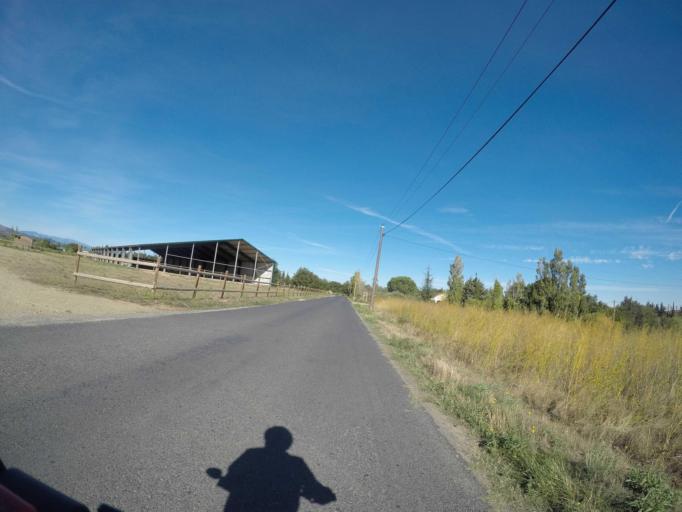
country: FR
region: Languedoc-Roussillon
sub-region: Departement des Pyrenees-Orientales
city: Ponteilla
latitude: 42.6400
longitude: 2.8051
